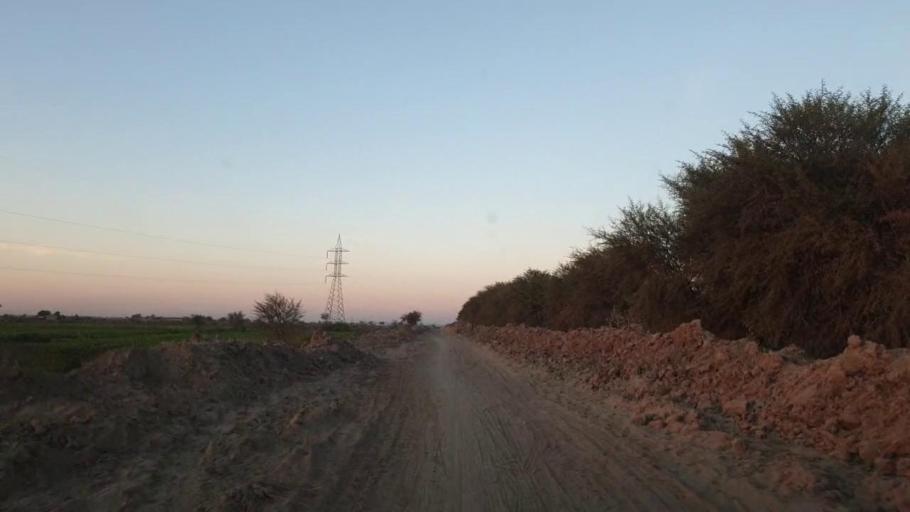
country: PK
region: Sindh
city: Kunri
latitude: 25.1517
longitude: 69.4468
